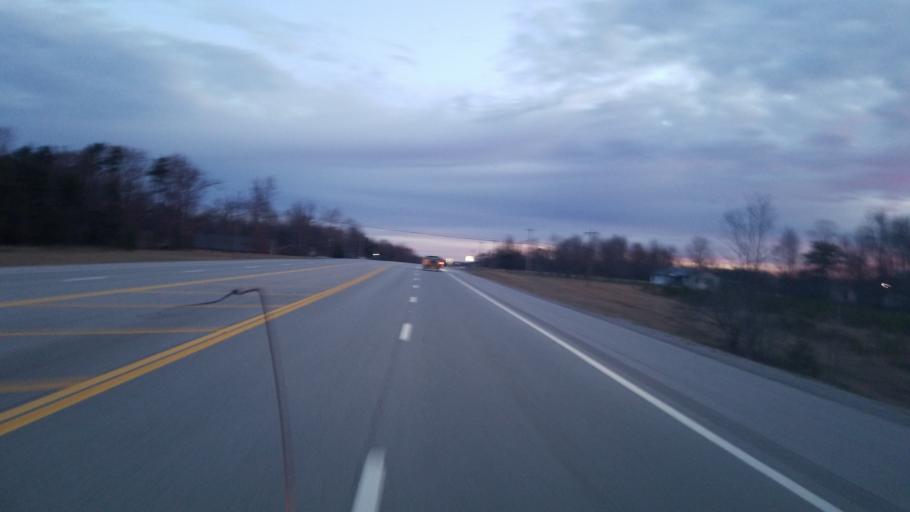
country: US
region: Tennessee
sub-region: Van Buren County
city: Spencer
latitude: 35.7243
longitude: -85.4675
